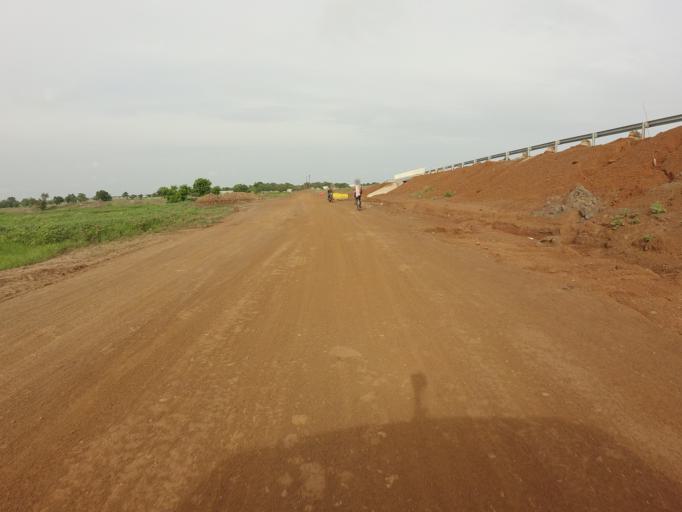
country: GH
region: Northern
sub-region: Yendi
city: Yendi
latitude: 9.9300
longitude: -0.2067
